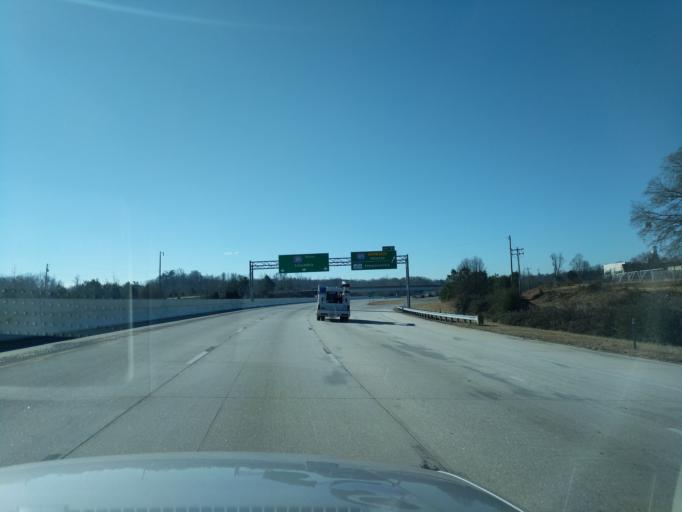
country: US
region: South Carolina
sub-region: Greenville County
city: Mauldin
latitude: 34.7723
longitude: -82.2729
